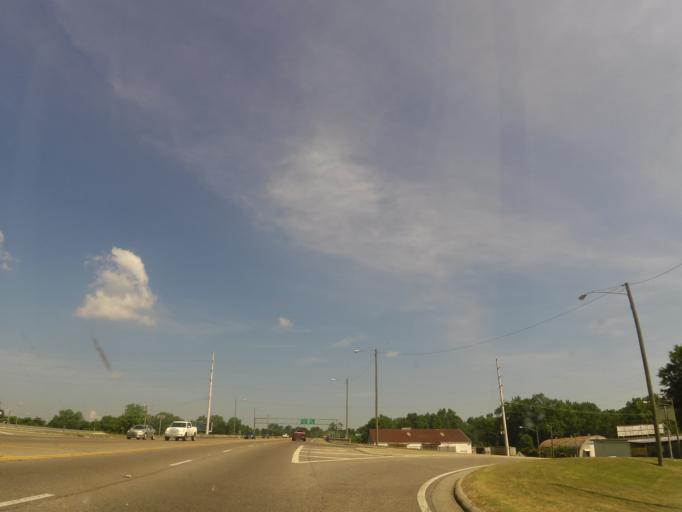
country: US
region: Mississippi
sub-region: Lauderdale County
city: Meridian
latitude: 32.3702
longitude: -88.6789
